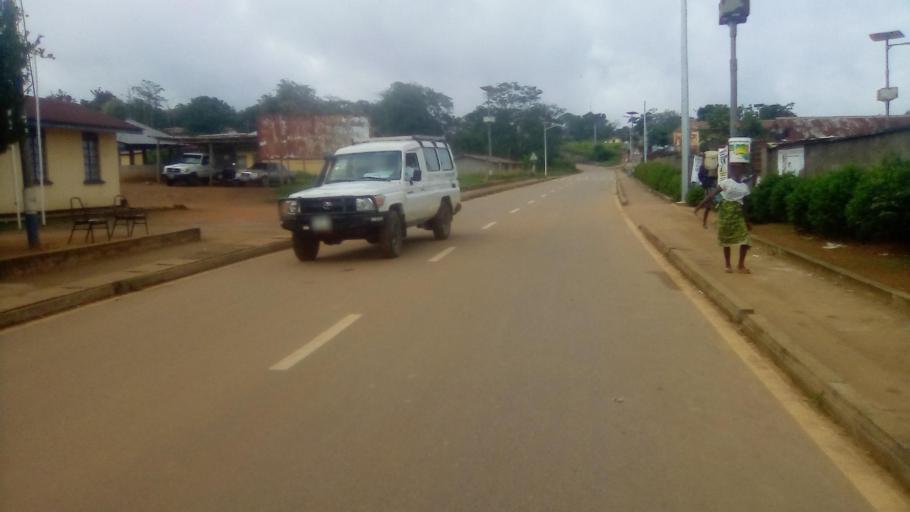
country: SL
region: Eastern Province
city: Kailahun
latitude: 8.2758
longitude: -10.5733
